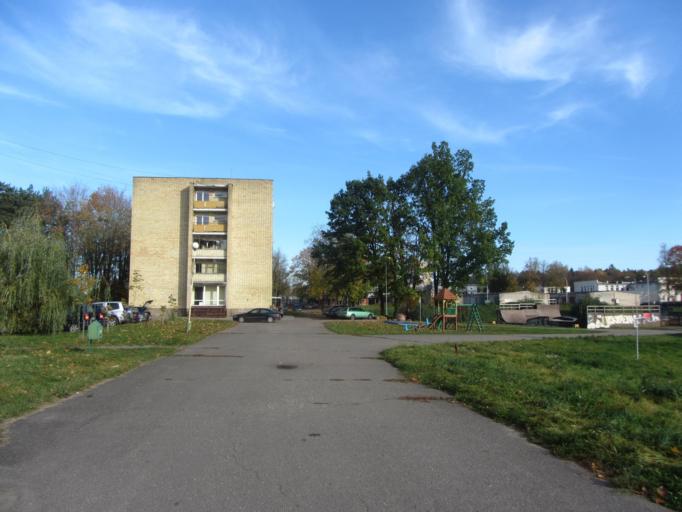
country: LT
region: Vilnius County
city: Elektrenai
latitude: 54.7826
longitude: 24.6558
